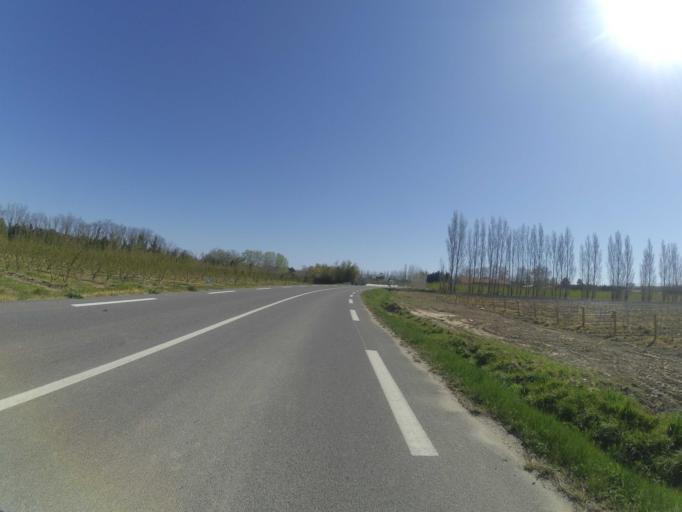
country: FR
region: Languedoc-Roussillon
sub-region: Departement des Pyrenees-Orientales
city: Millas
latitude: 42.6835
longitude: 2.6935
